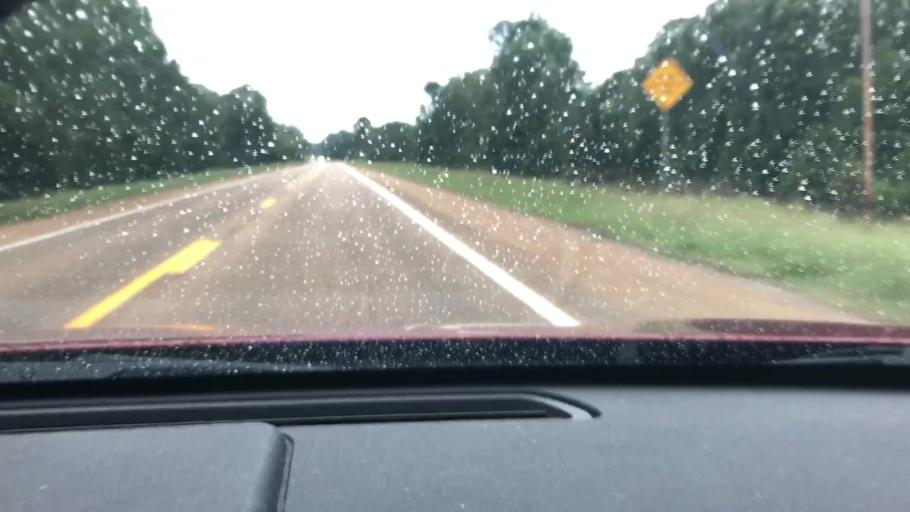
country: US
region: Arkansas
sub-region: Lafayette County
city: Stamps
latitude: 33.3588
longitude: -93.4113
